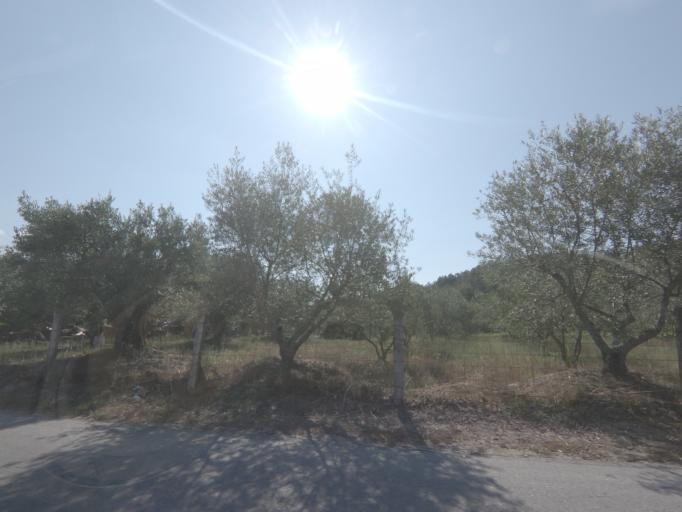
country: PT
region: Viseu
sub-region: Moimenta da Beira
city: Moimenta da Beira
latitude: 40.9932
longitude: -7.5611
